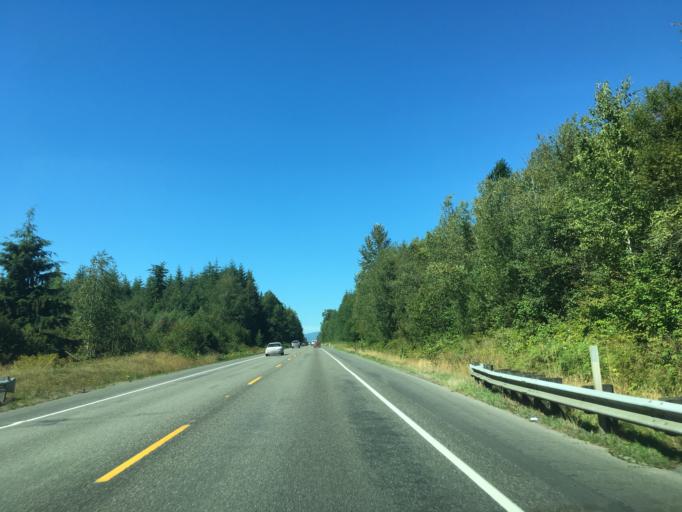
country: US
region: Washington
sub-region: Snohomish County
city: Sisco Heights
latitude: 48.1283
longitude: -122.1127
